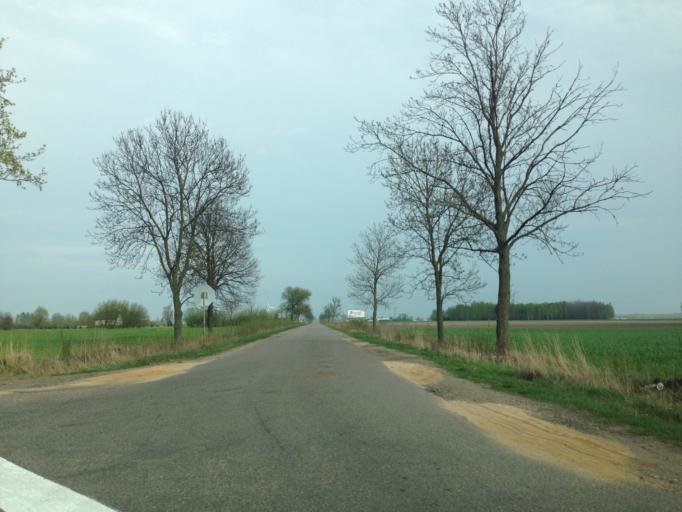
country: PL
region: Masovian Voivodeship
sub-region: Powiat zurominski
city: Biezun
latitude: 52.9836
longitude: 19.9591
